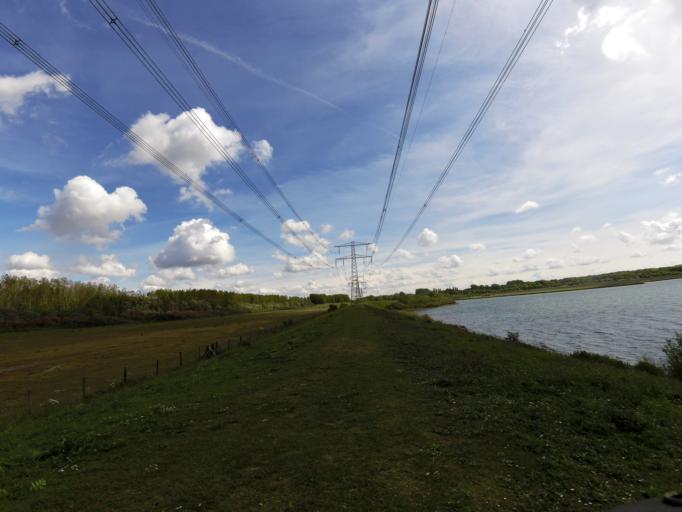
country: NL
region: South Holland
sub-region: Gemeente Rotterdam
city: Hoek van Holland
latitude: 51.9305
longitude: 4.0950
